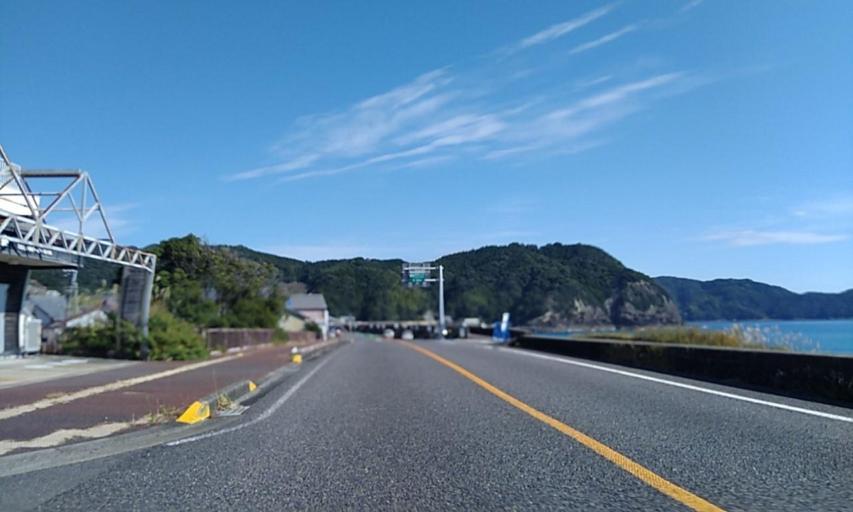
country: JP
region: Wakayama
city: Shingu
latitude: 33.8869
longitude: 136.1009
